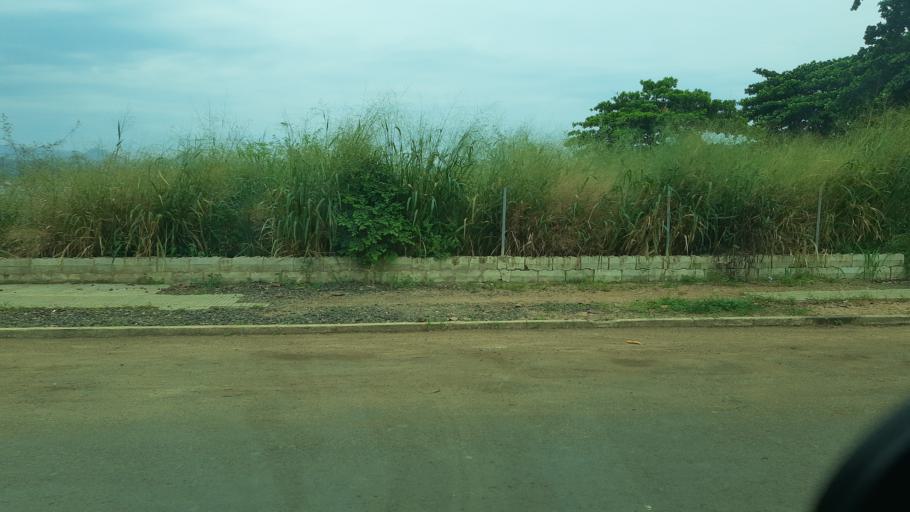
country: ST
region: Sao Tome Island
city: Sao Tome
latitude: 0.3425
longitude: 6.7356
